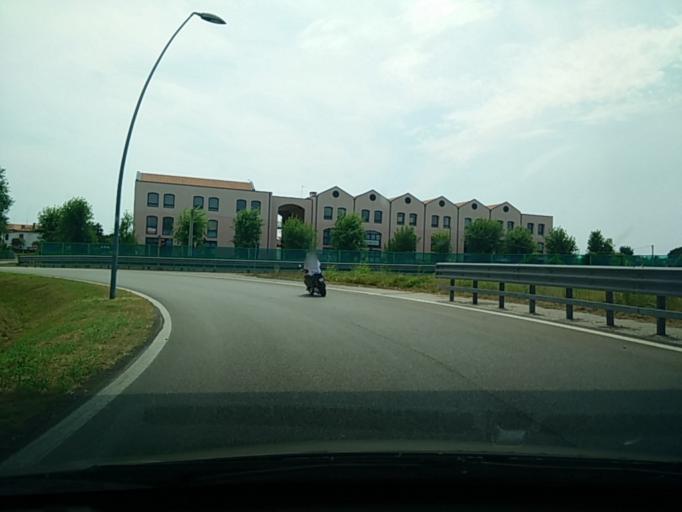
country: IT
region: Veneto
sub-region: Provincia di Treviso
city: Silea
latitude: 45.6571
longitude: 12.2849
